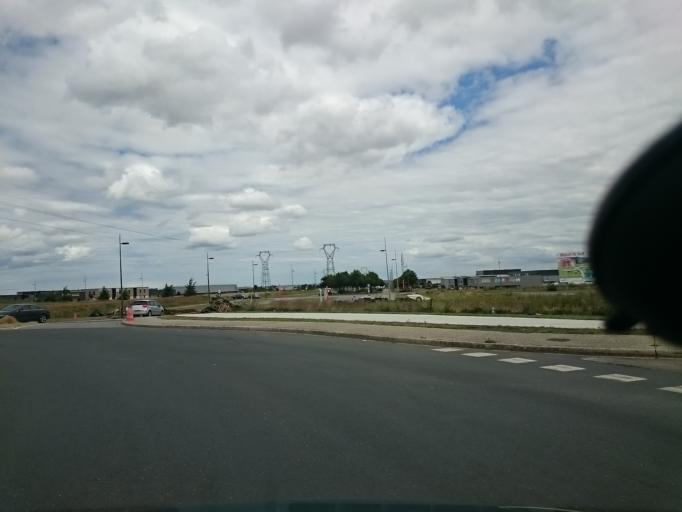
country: FR
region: Lower Normandy
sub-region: Departement du Calvados
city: Cormelles-le-Royal
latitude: 49.1383
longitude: -0.3314
